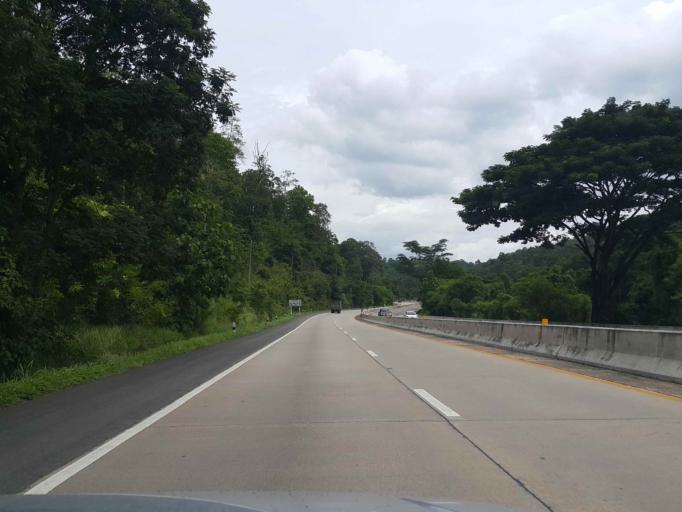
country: TH
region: Lamphun
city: Mae Tha
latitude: 18.3835
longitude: 99.2213
